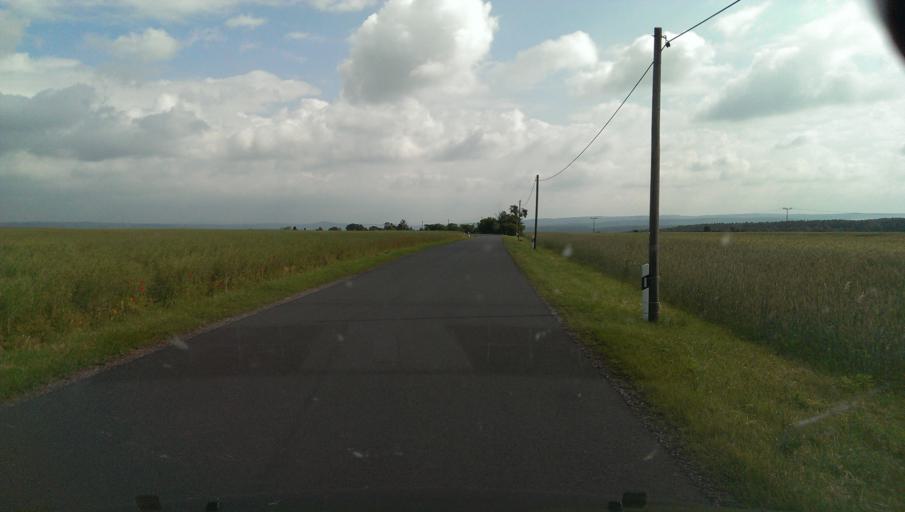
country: DE
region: Thuringia
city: Rittersdorf
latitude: 50.8248
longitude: 11.2382
